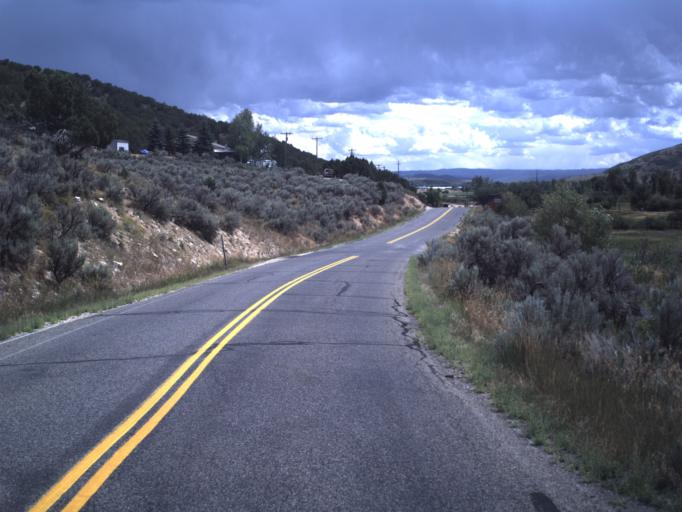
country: US
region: Utah
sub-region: Summit County
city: Oakley
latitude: 40.7568
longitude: -111.3739
